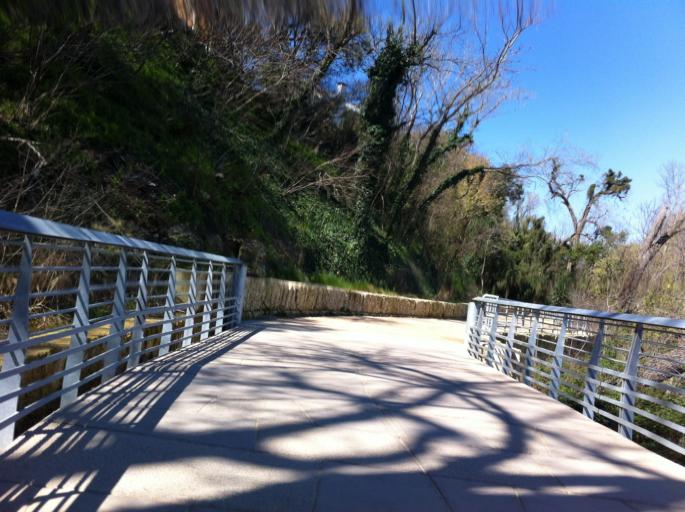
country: US
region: Texas
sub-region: Travis County
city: Austin
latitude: 30.2508
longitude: -97.7385
